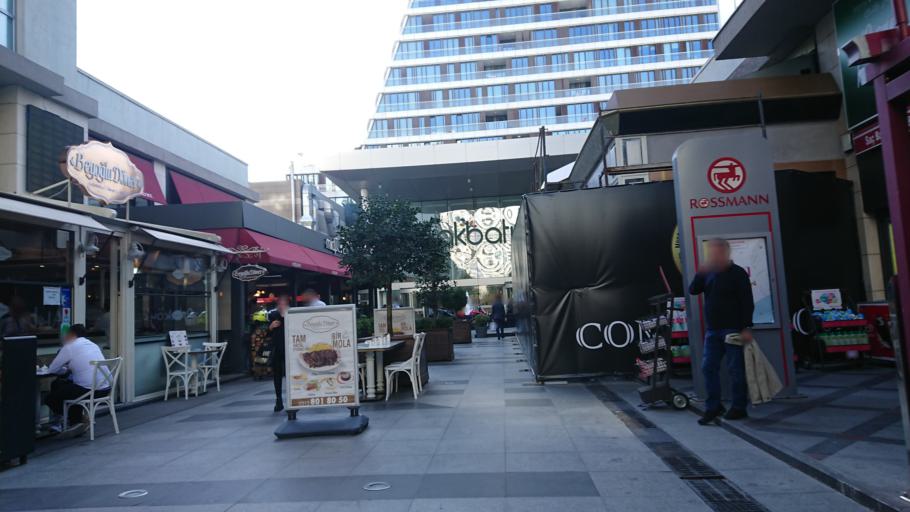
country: TR
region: Istanbul
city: Esenyurt
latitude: 41.0579
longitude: 28.6684
